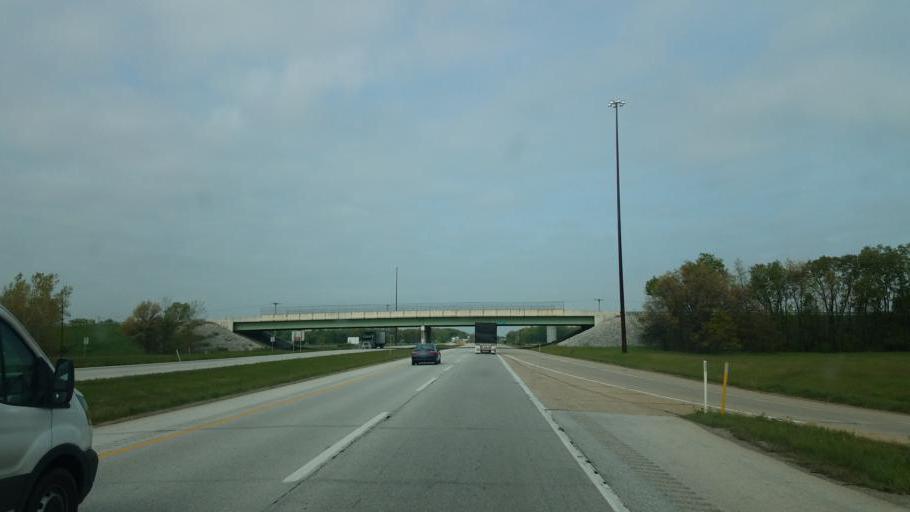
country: US
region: Indiana
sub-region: Elkhart County
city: Bristol
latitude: 41.7306
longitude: -85.8865
